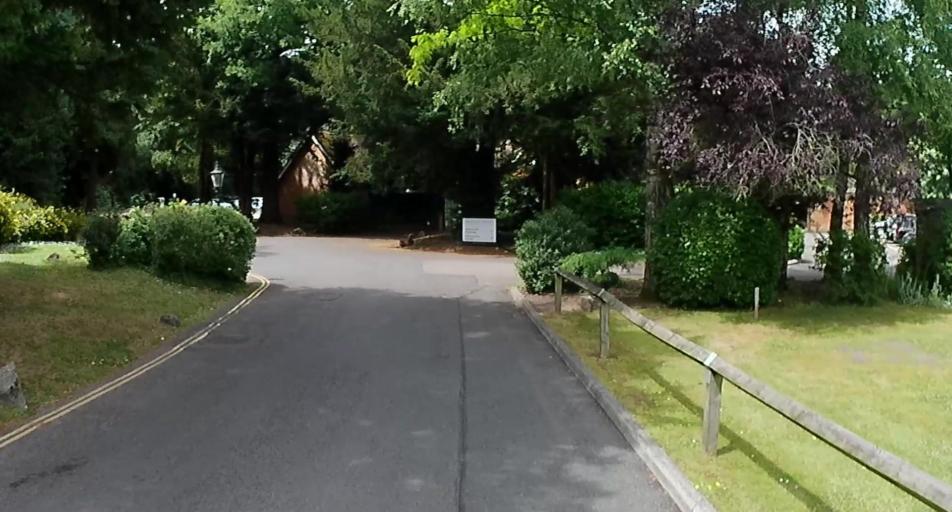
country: GB
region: England
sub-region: Hampshire
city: Basingstoke
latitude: 51.2454
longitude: -1.0830
